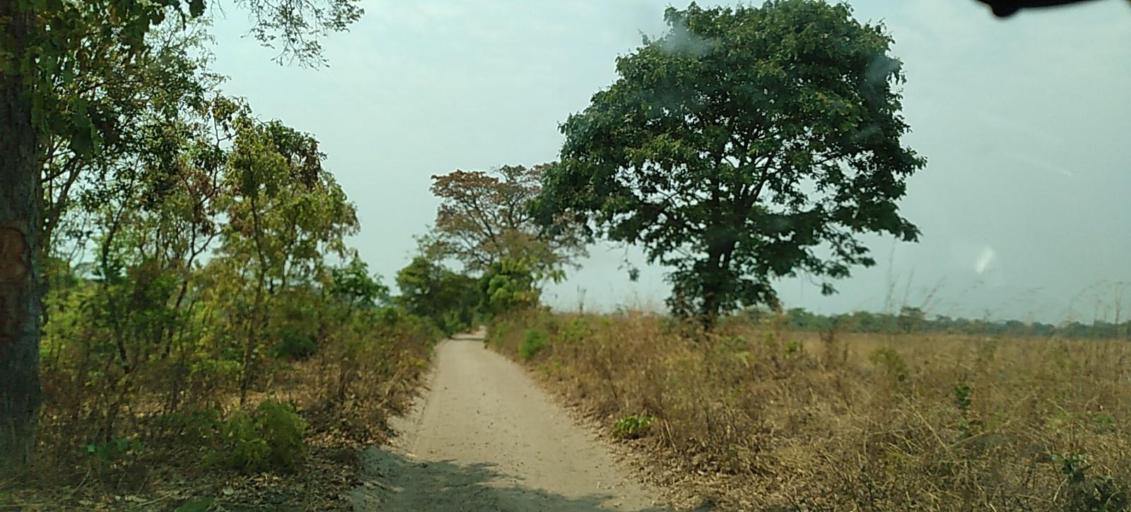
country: ZM
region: North-Western
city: Kabompo
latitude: -13.4654
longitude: 24.4348
